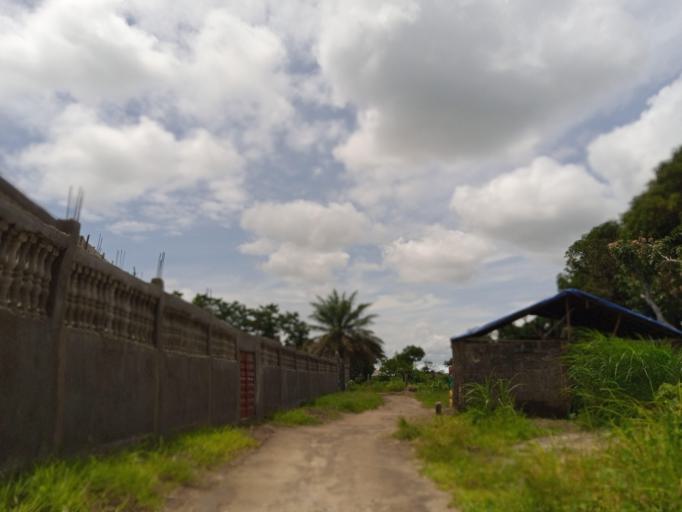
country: SL
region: Northern Province
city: Masoyila
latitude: 8.5925
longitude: -13.1831
